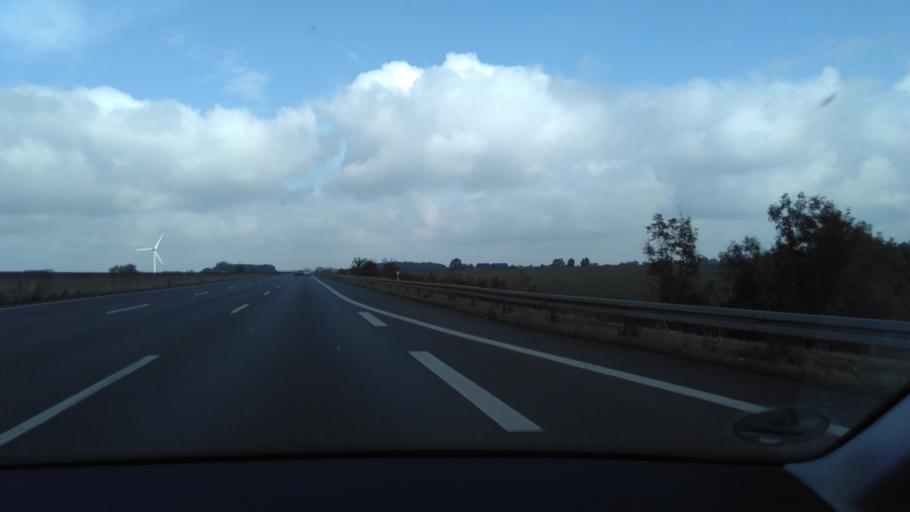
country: DE
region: North Rhine-Westphalia
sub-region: Regierungsbezirk Munster
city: Beckum
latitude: 51.7267
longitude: 7.9818
